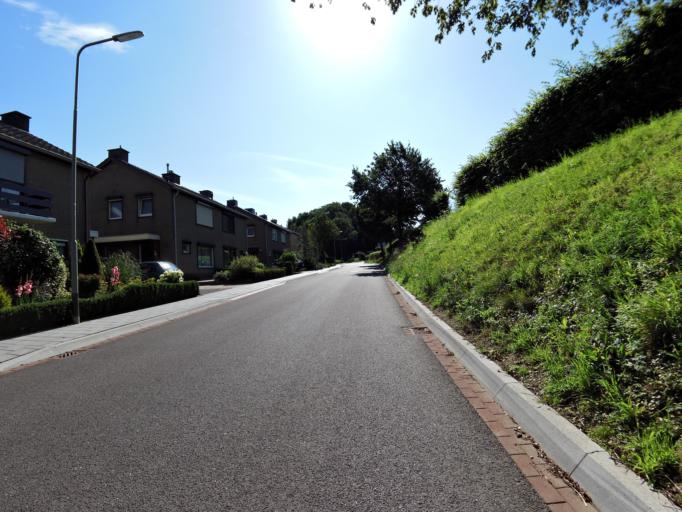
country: NL
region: Limburg
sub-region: Gemeente Voerendaal
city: Ubachsberg
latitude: 50.8239
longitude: 5.9416
